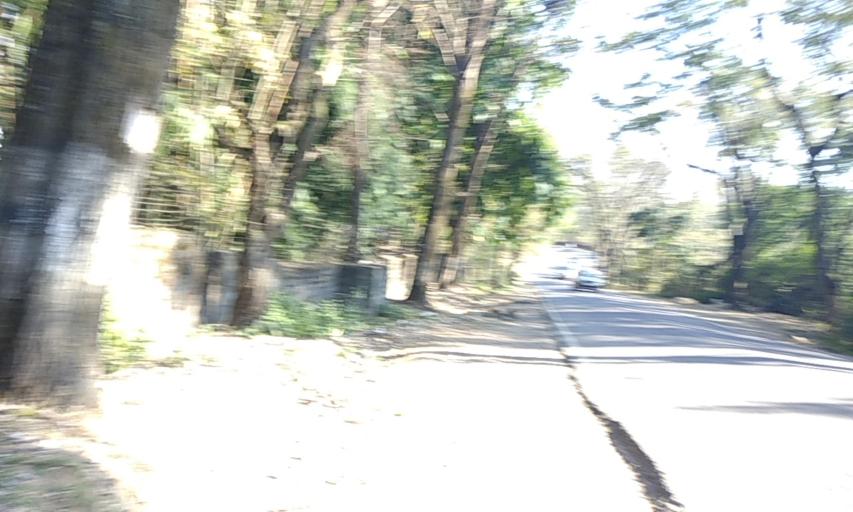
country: IN
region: Himachal Pradesh
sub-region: Kangra
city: Palampur
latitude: 32.1043
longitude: 76.5541
